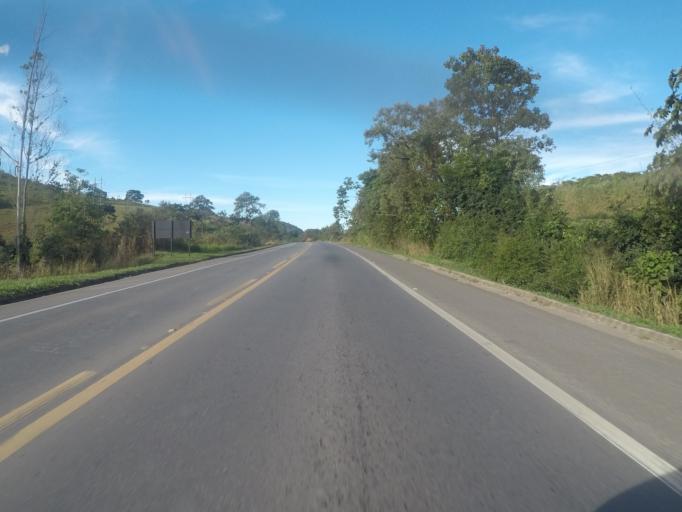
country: BR
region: Espirito Santo
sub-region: Ibiracu
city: Ibiracu
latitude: -19.8666
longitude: -40.3990
